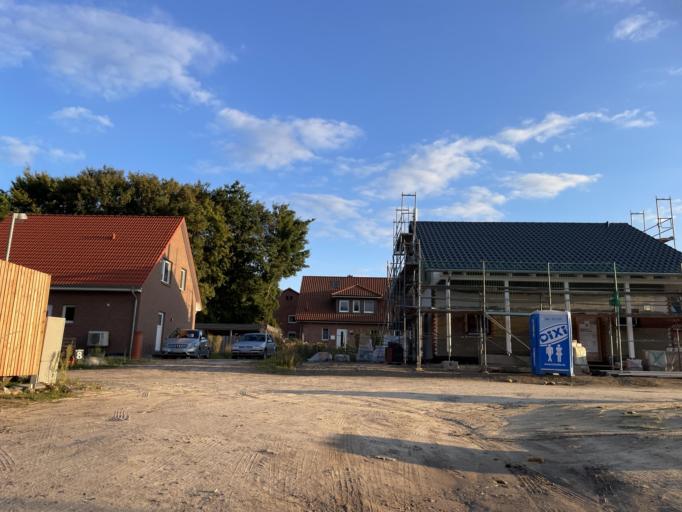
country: DE
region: Lower Saxony
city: Wendisch Evern
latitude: 53.2168
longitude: 10.4721
